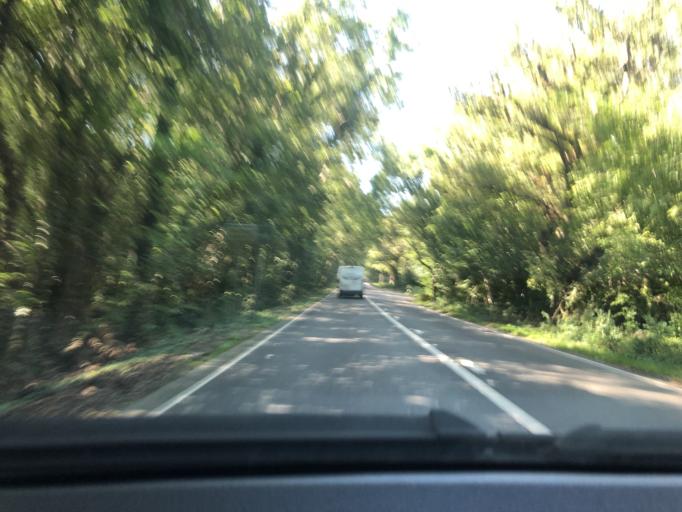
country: GB
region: England
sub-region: Somerset
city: Westonzoyland
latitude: 51.1335
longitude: -2.8516
